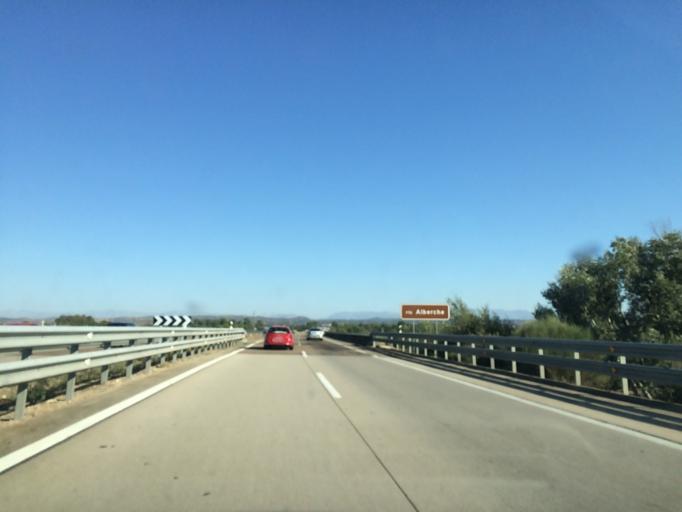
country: ES
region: Castille-La Mancha
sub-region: Province of Toledo
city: Talavera de la Reina
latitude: 39.9852
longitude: -4.7552
